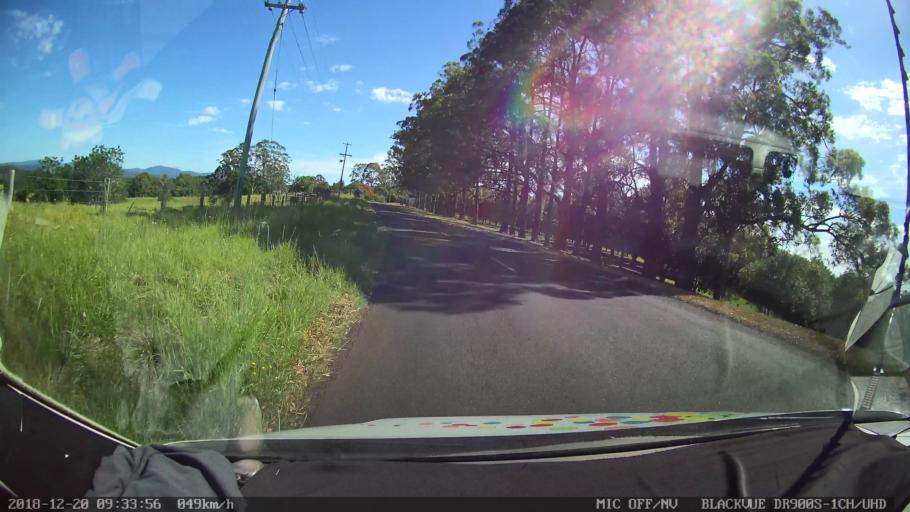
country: AU
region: New South Wales
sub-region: Lismore Municipality
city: Goonellabah
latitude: -28.6937
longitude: 153.3119
